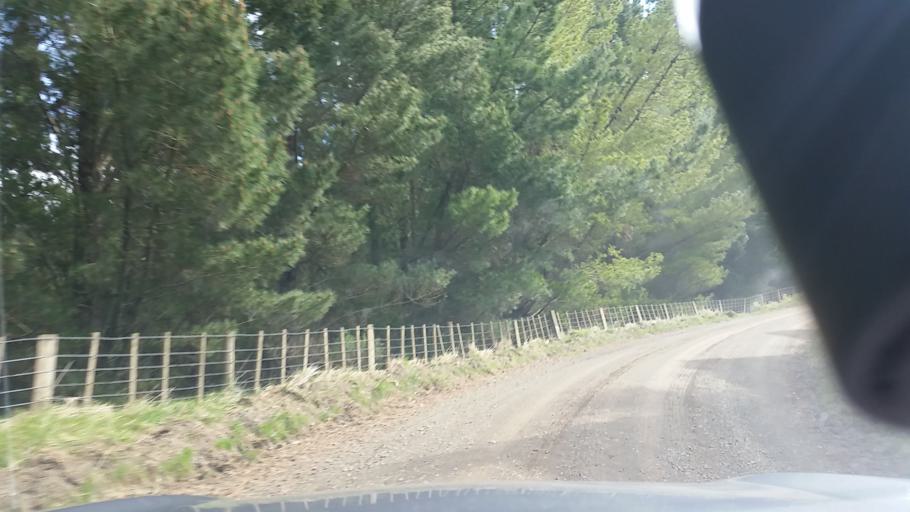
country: NZ
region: Hawke's Bay
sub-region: Napier City
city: Napier
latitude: -39.2177
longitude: 176.9831
